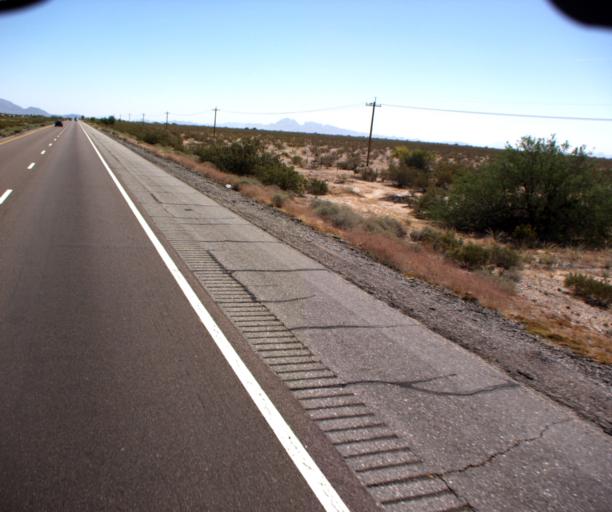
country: US
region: Arizona
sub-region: La Paz County
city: Salome
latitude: 33.5600
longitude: -113.2955
